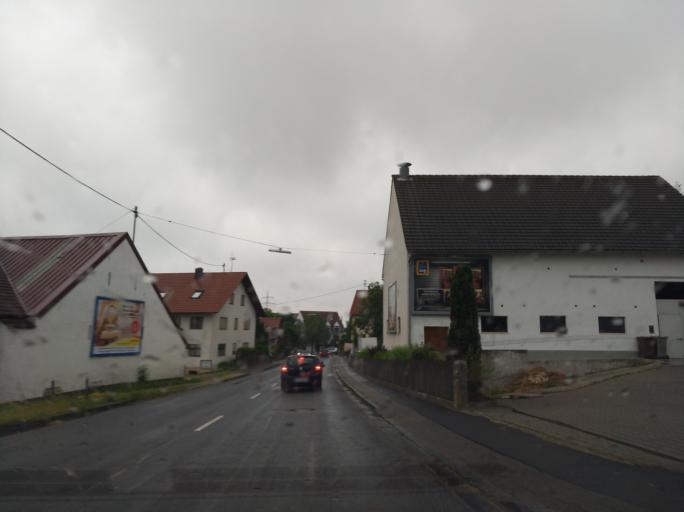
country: DE
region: Bavaria
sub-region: Swabia
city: Rehling
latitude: 48.4405
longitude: 10.9385
